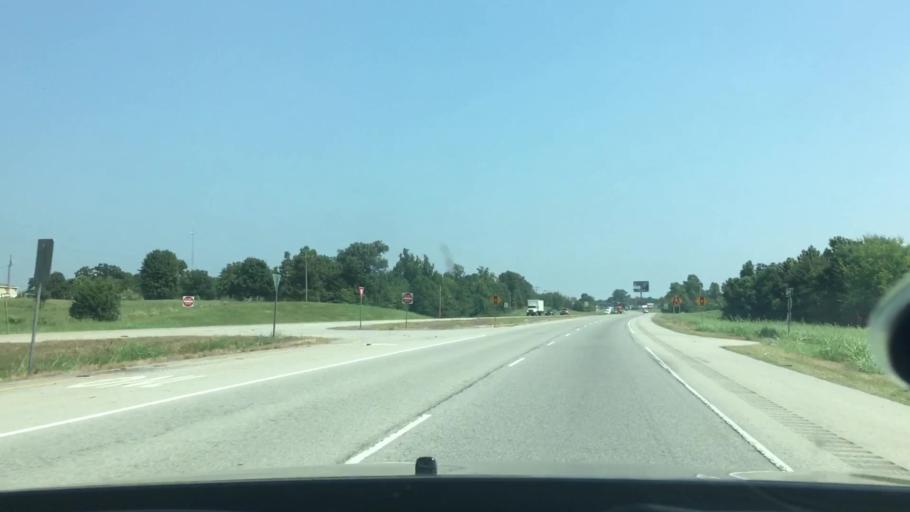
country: US
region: Oklahoma
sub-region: Atoka County
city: Atoka
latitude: 34.3097
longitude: -96.1750
